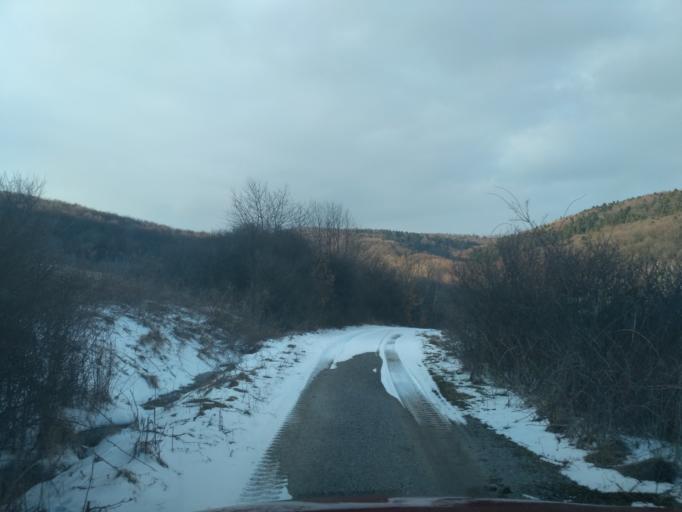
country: SK
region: Kosicky
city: Kosice
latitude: 48.7427
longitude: 21.1502
